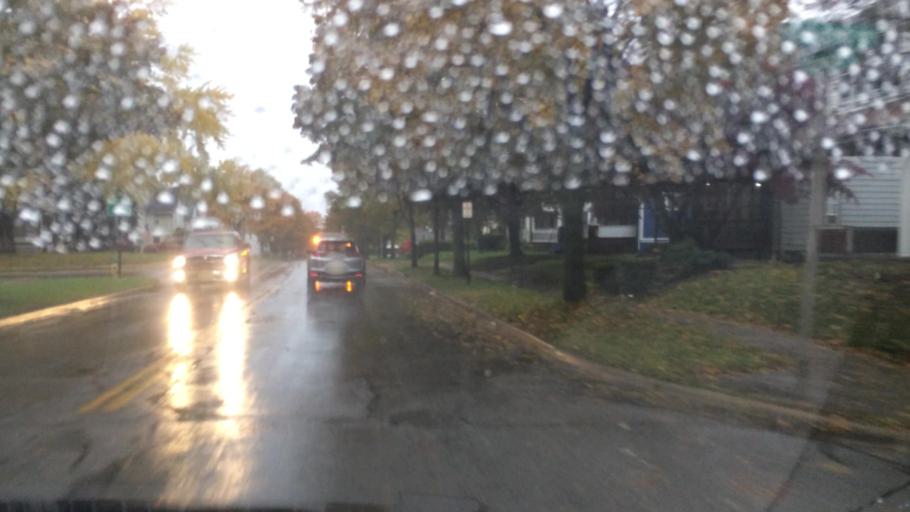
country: US
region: Ohio
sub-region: Summit County
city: Akron
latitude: 41.0467
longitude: -81.5154
